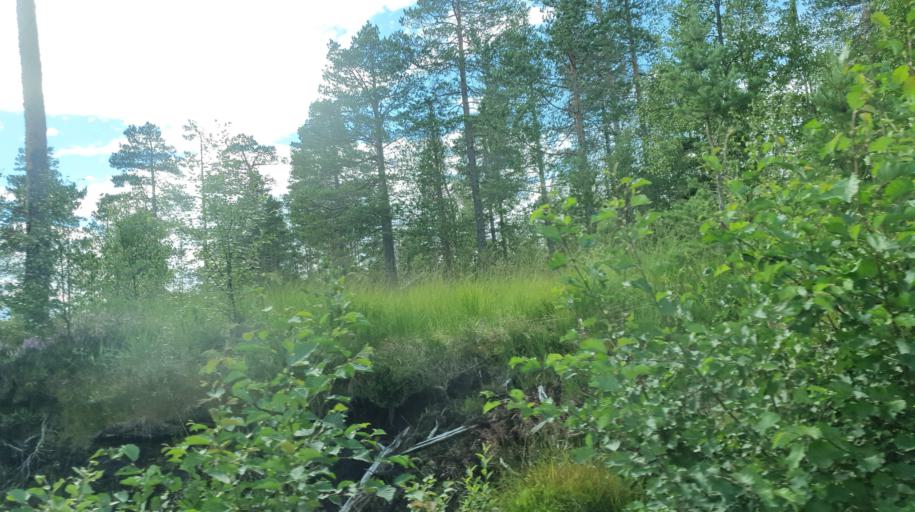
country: NO
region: Nord-Trondelag
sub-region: Levanger
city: Skogn
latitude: 63.5836
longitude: 11.2447
